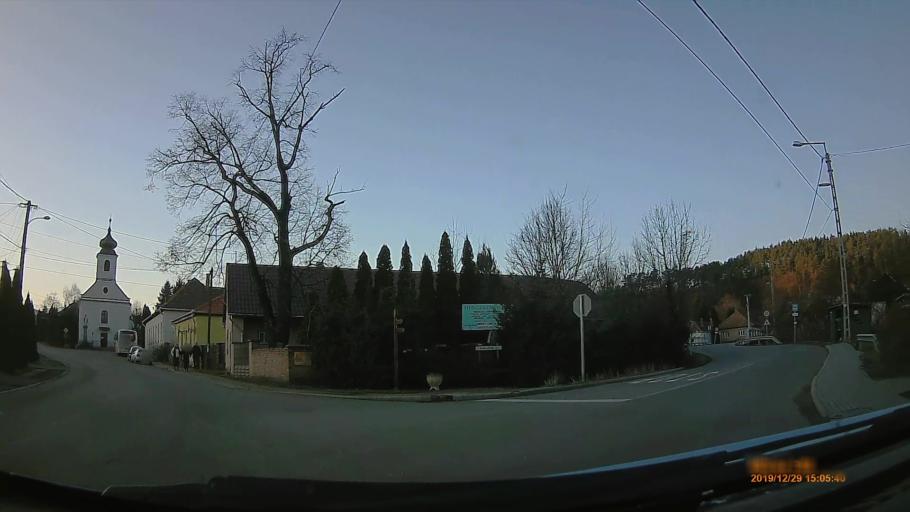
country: HU
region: Heves
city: Parad
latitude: 47.9240
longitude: 20.0266
